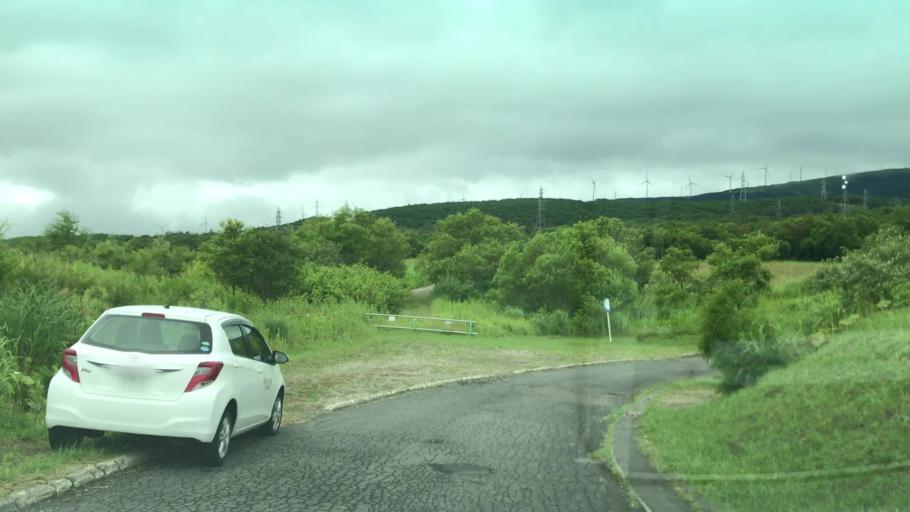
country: JP
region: Hokkaido
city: Muroran
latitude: 42.3928
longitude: 141.0000
